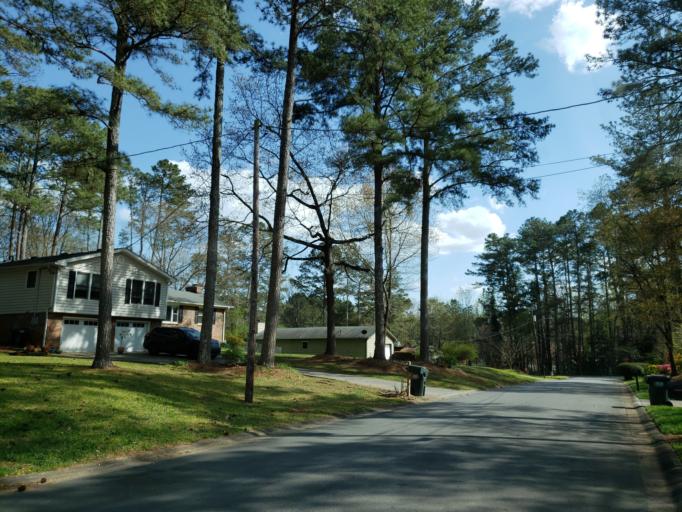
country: US
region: Georgia
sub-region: Cherokee County
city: Woodstock
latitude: 34.0355
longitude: -84.4786
